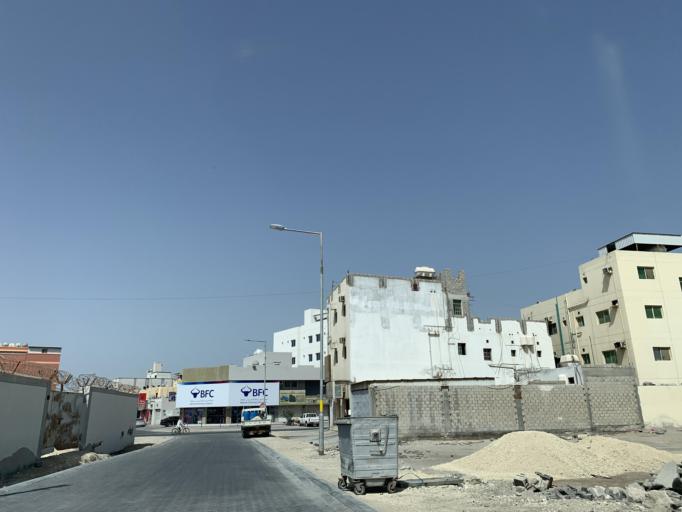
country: BH
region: Northern
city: Sitrah
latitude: 26.1441
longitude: 50.6028
